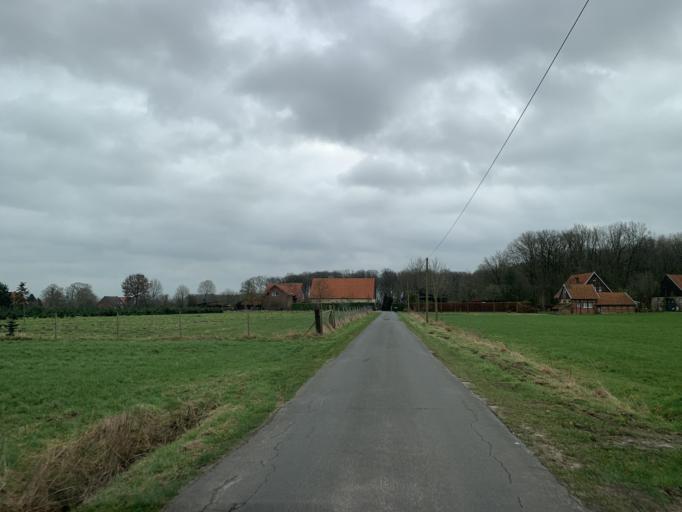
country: DE
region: North Rhine-Westphalia
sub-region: Regierungsbezirk Munster
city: Dulmen
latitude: 51.8513
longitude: 7.3200
